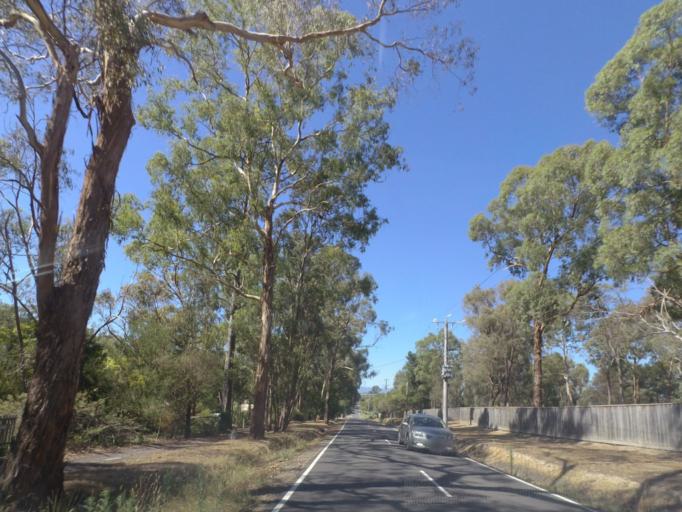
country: AU
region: Victoria
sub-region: Yarra Ranges
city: Chirnside Park
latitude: -37.7420
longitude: 145.2784
